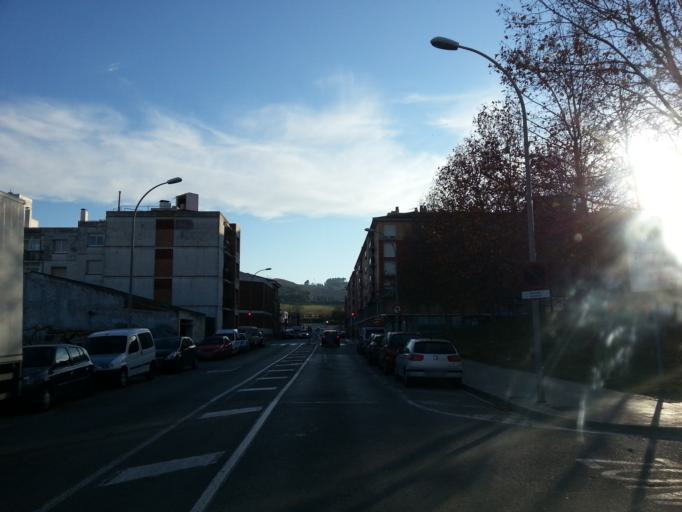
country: ES
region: Catalonia
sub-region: Provincia de Barcelona
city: Terrassa
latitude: 41.5583
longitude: 1.9946
